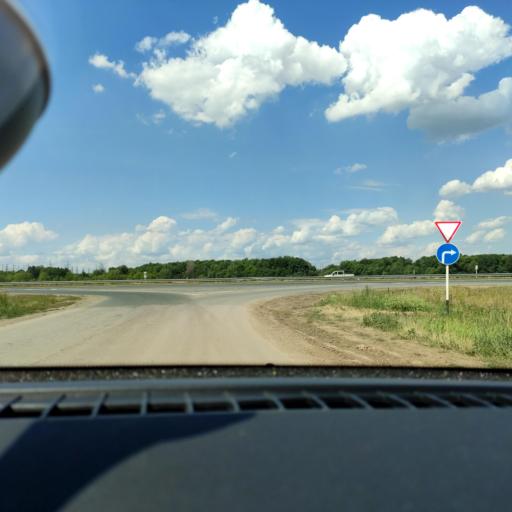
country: RU
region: Samara
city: Kinel'
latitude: 53.2617
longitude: 50.5257
